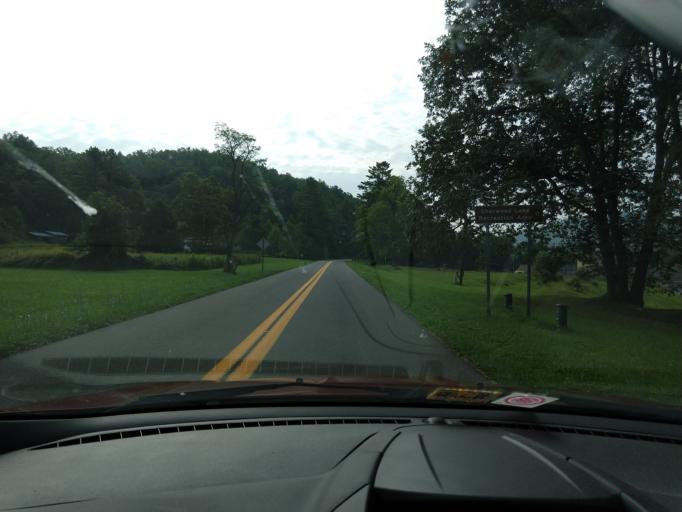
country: US
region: Virginia
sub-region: City of Covington
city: Covington
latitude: 37.9652
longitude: -80.1272
